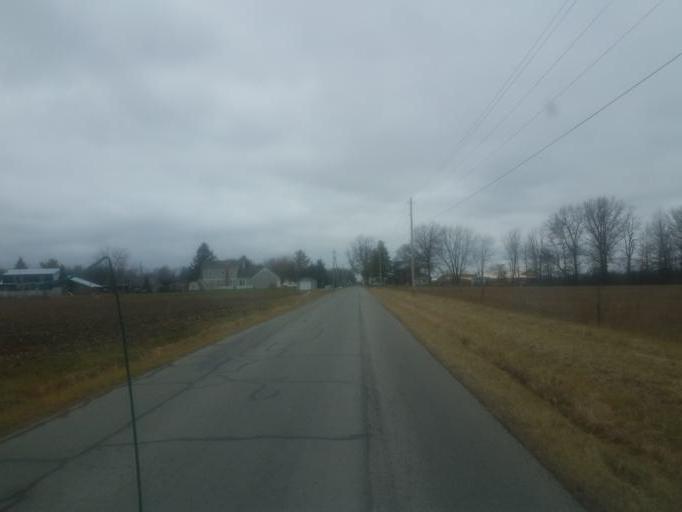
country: US
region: Ohio
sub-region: Crawford County
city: Crestline
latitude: 40.7991
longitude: -82.7385
